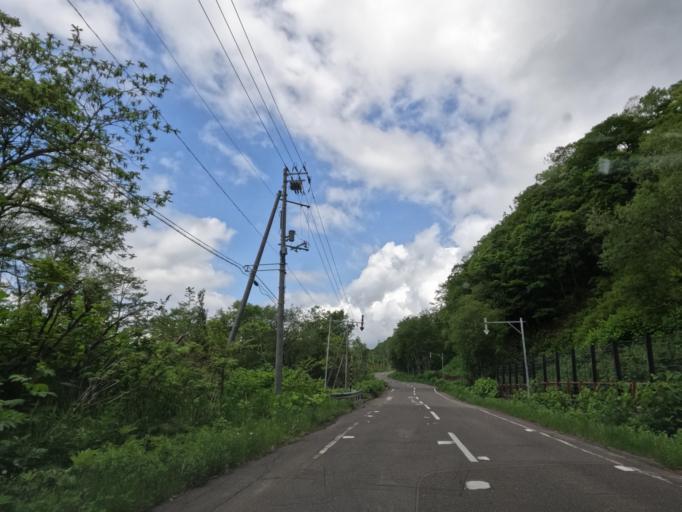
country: JP
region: Hokkaido
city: Tobetsu
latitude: 43.4828
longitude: 141.6029
